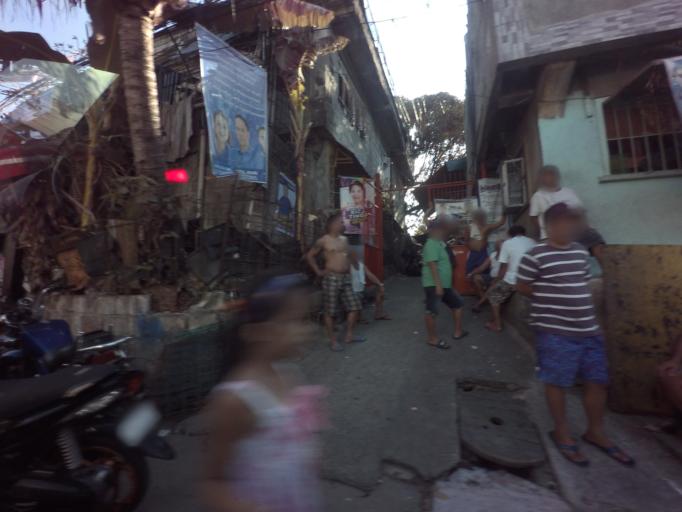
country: PH
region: Calabarzon
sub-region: Province of Rizal
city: Taguig
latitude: 14.4936
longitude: 121.0480
